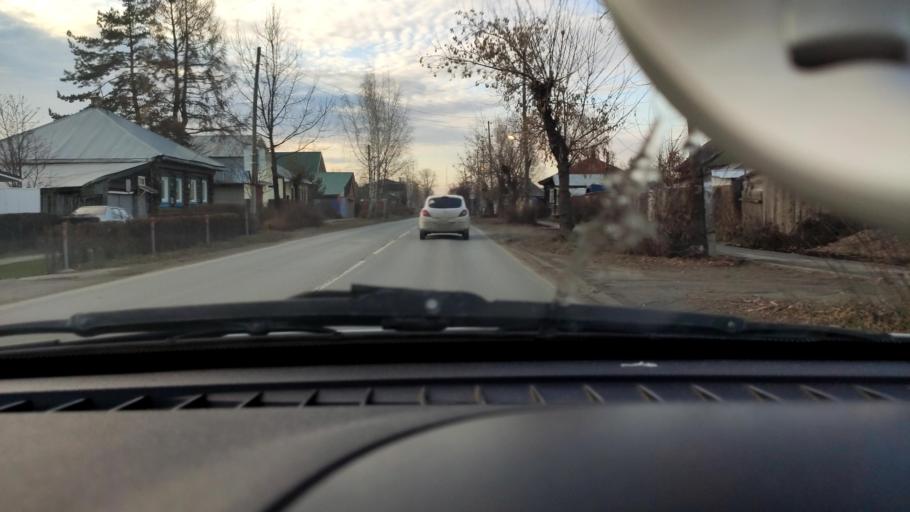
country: RU
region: Perm
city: Perm
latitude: 58.0469
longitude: 56.3310
